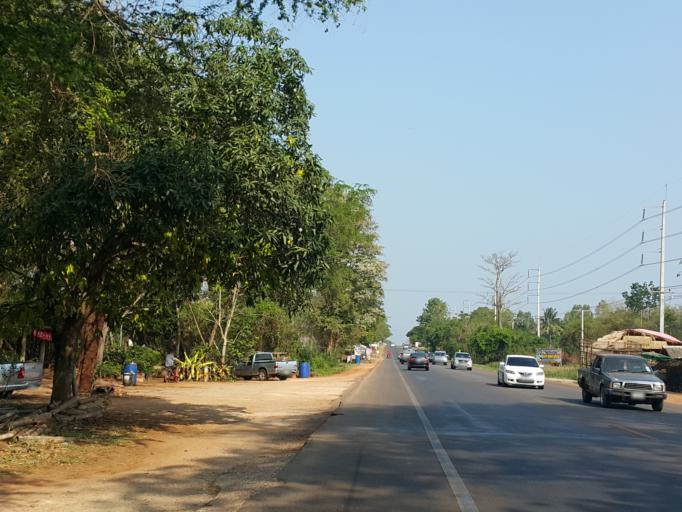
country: TH
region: Kanchanaburi
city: Sai Yok
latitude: 14.1240
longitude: 99.1750
